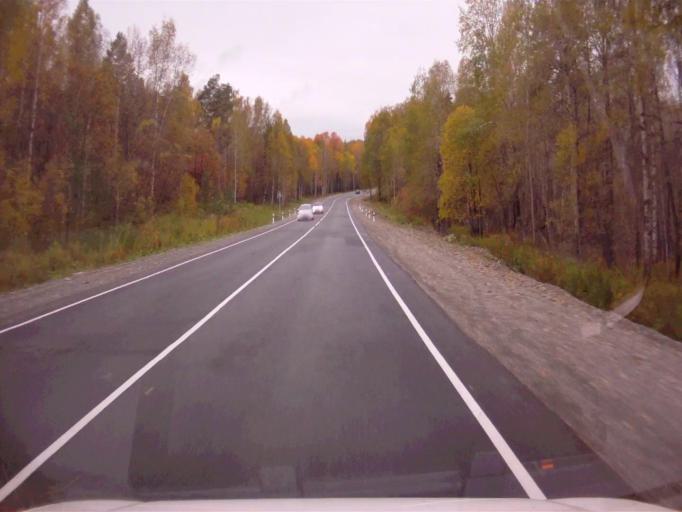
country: RU
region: Chelyabinsk
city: Nyazepetrovsk
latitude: 56.0664
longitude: 59.6996
